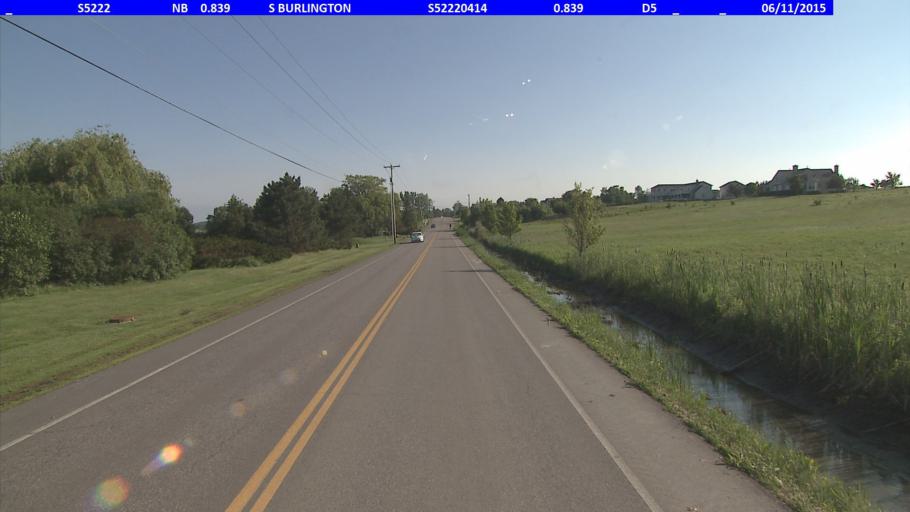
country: US
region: Vermont
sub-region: Chittenden County
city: South Burlington
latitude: 44.4288
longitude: -73.1937
